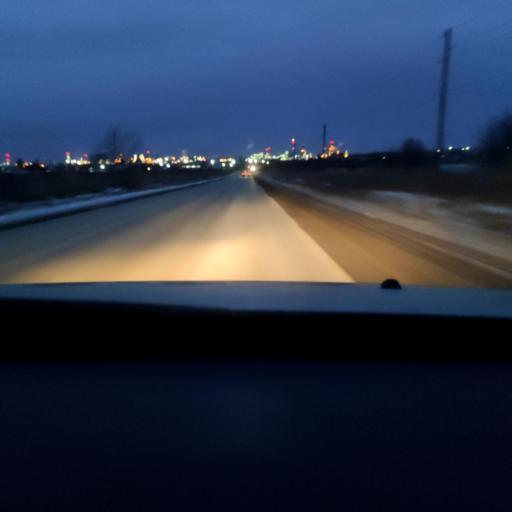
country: RU
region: Perm
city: Gamovo
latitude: 57.8881
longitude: 56.1082
